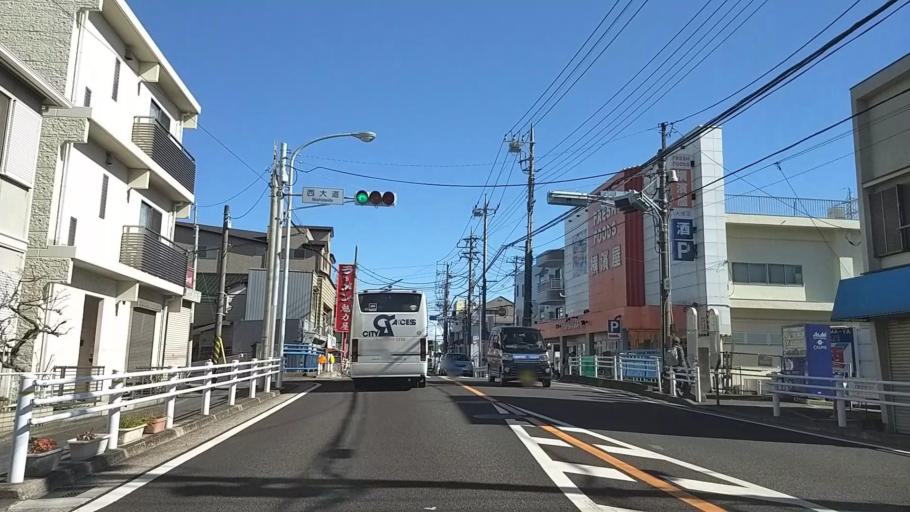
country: JP
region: Kanagawa
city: Zushi
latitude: 35.3289
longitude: 139.6049
